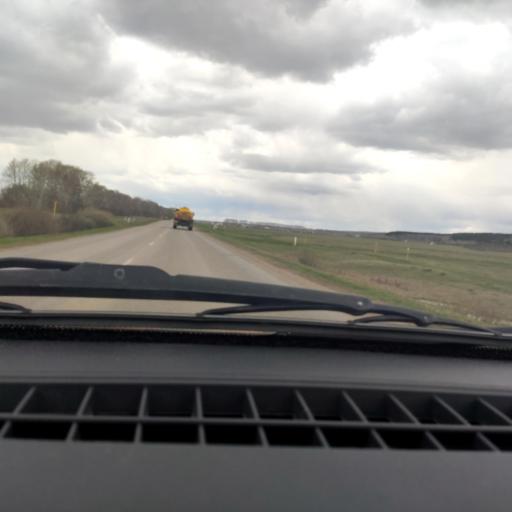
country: RU
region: Bashkortostan
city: Chekmagush
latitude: 55.1260
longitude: 54.7055
